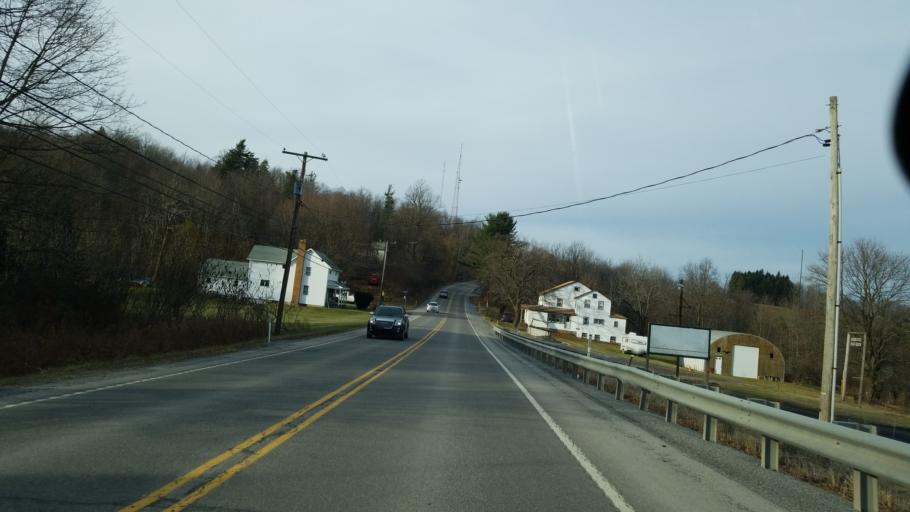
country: US
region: Pennsylvania
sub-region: Clearfield County
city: Sandy
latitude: 41.0410
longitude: -78.7001
